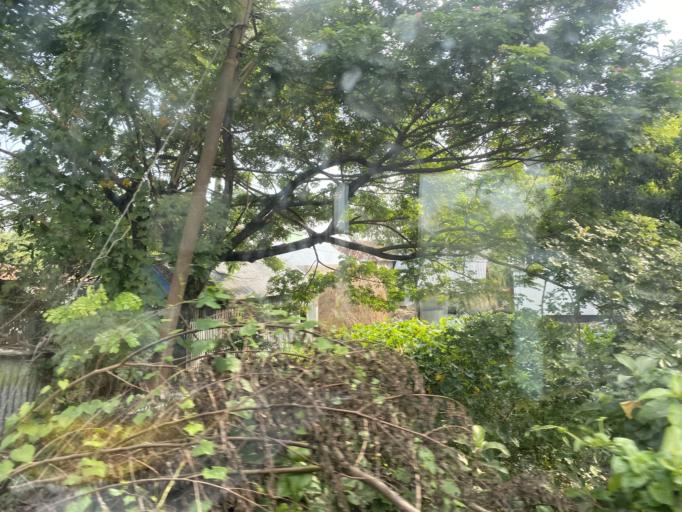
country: BD
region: Chittagong
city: Nabinagar
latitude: 23.9539
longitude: 91.1196
